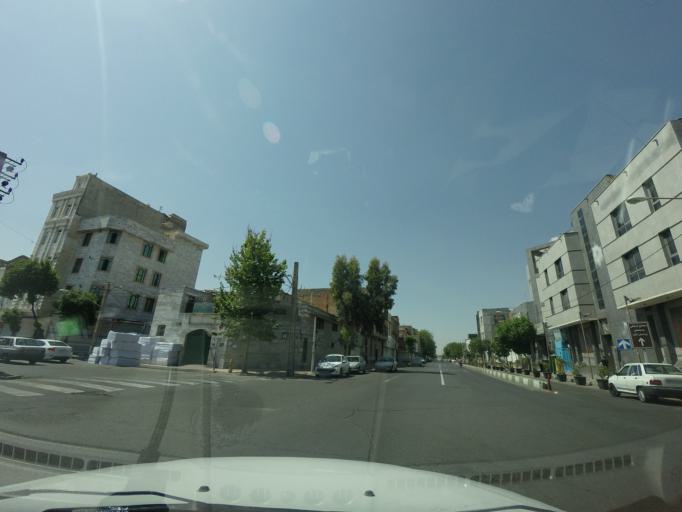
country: IR
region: Tehran
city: Tehran
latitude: 35.6395
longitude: 51.3659
